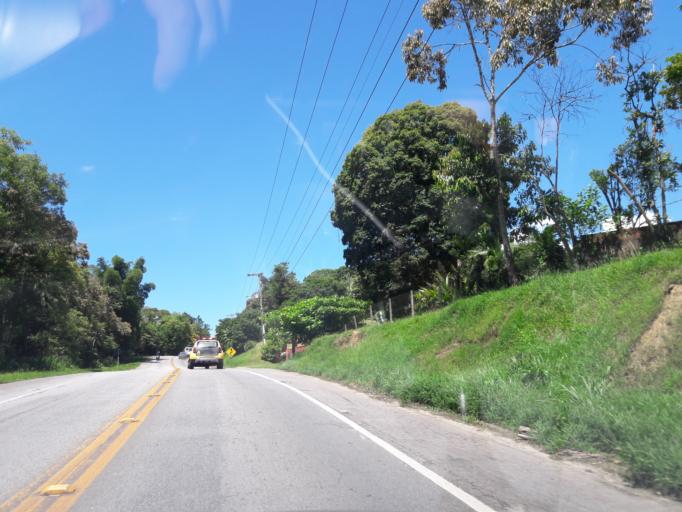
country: BR
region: Parana
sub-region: Antonina
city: Antonina
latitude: -25.5116
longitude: -48.8101
